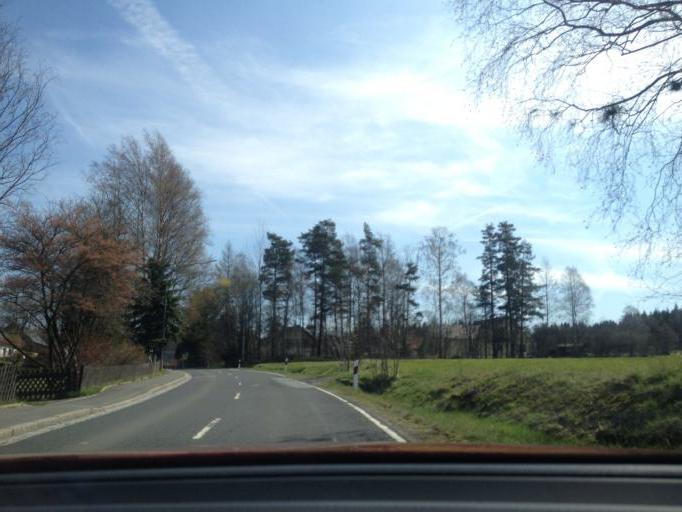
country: DE
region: Bavaria
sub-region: Upper Franconia
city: Weissenstadt
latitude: 50.0823
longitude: 11.8569
